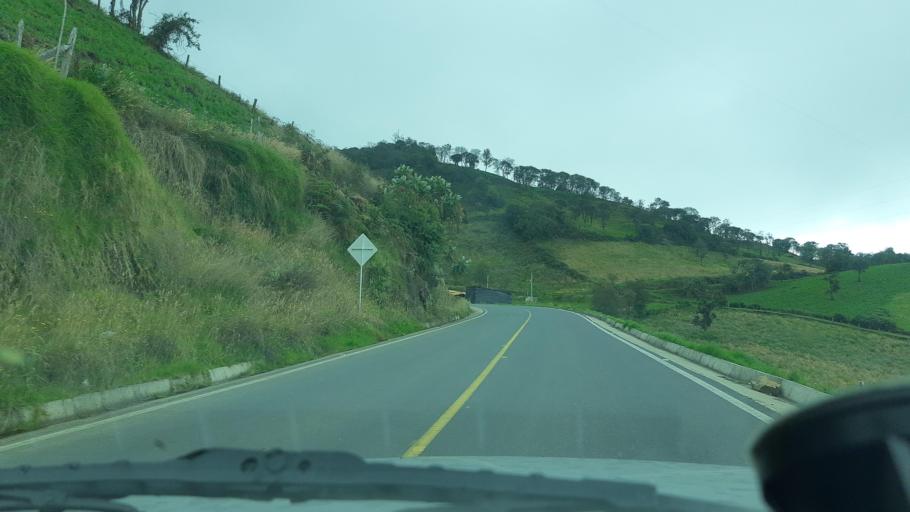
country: CO
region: Cundinamarca
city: Umbita
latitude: 5.2277
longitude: -73.4721
